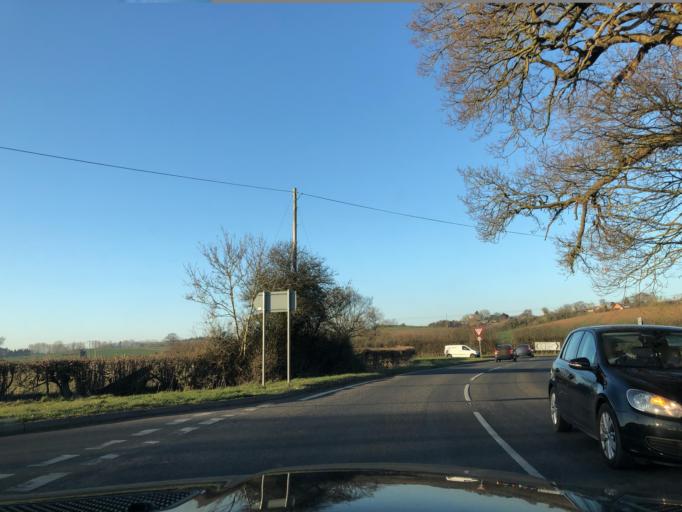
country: GB
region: England
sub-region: Warwickshire
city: Warwick
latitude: 52.2715
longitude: -1.6341
